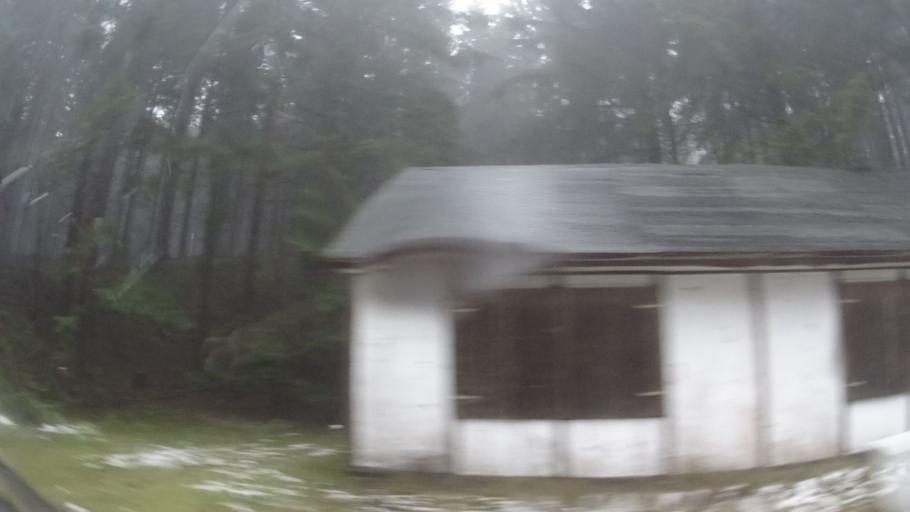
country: DE
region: Thuringia
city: Eisfeld
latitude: 50.5044
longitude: 10.9044
